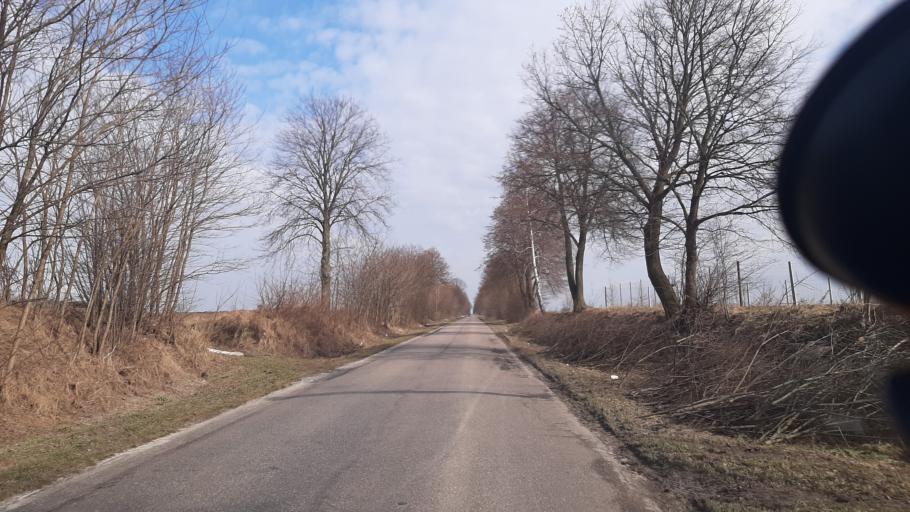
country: PL
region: Lublin Voivodeship
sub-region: Powiat lubartowski
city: Wola Sernicka
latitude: 51.4541
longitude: 22.6780
